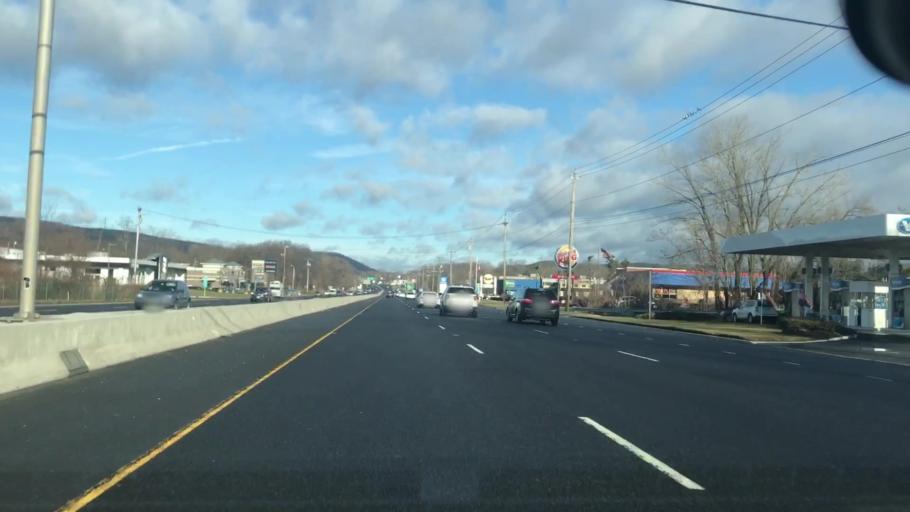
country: US
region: New Jersey
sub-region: Bergen County
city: Mahwah
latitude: 41.0825
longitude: -74.1507
